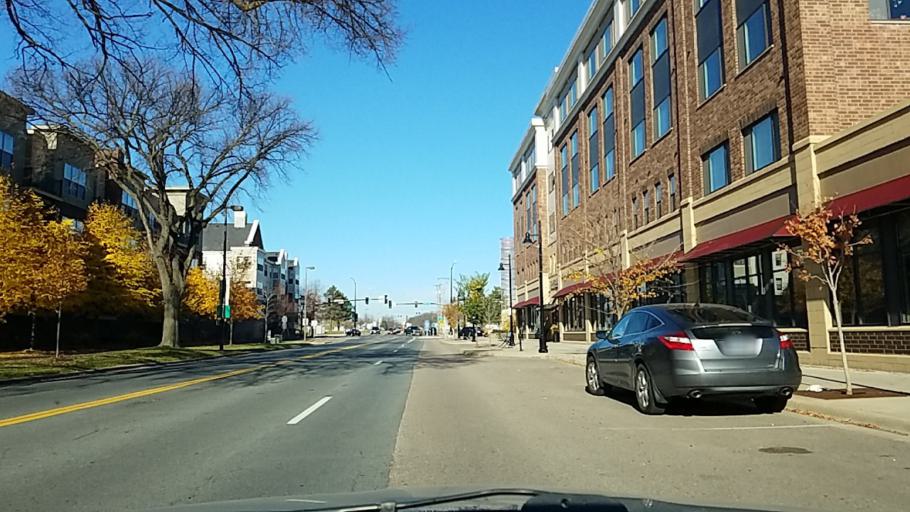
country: US
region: Minnesota
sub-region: Hennepin County
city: Saint Louis Park
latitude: 44.9368
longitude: -93.3537
